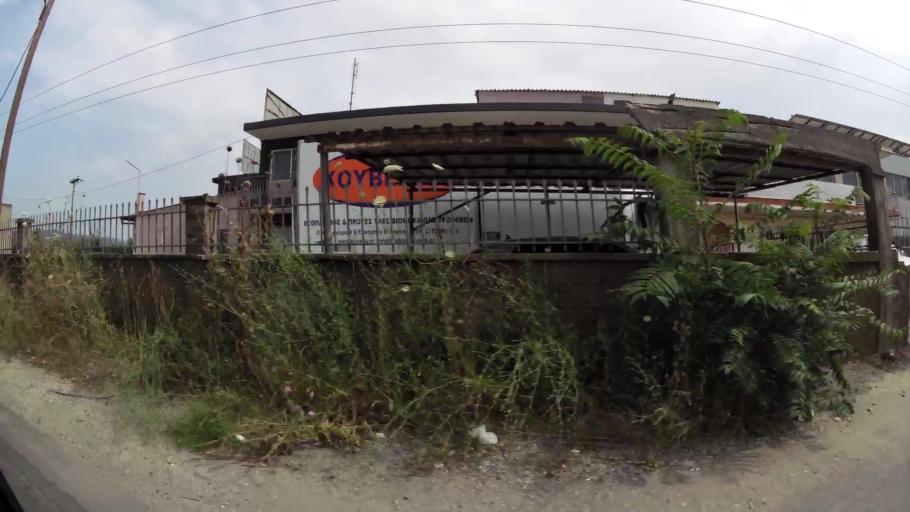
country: GR
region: Central Macedonia
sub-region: Nomos Thessalonikis
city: Efkarpia
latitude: 40.6916
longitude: 22.9321
